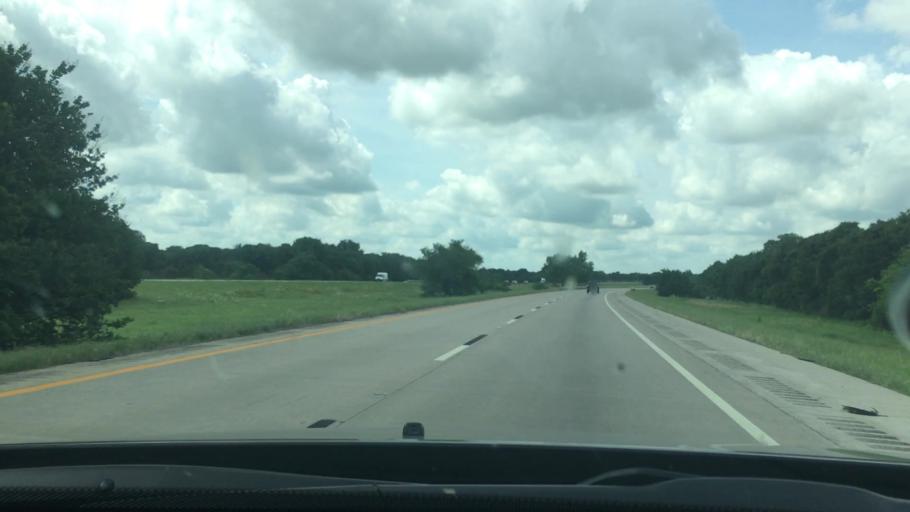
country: US
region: Oklahoma
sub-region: Love County
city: Marietta
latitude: 33.8271
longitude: -97.1304
